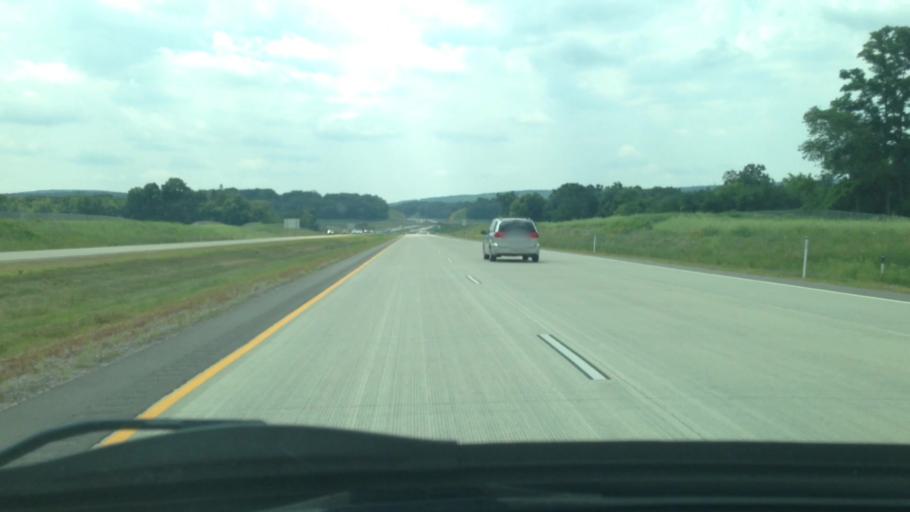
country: US
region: Wisconsin
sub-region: Sauk County
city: West Baraboo
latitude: 43.4537
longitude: -89.7782
